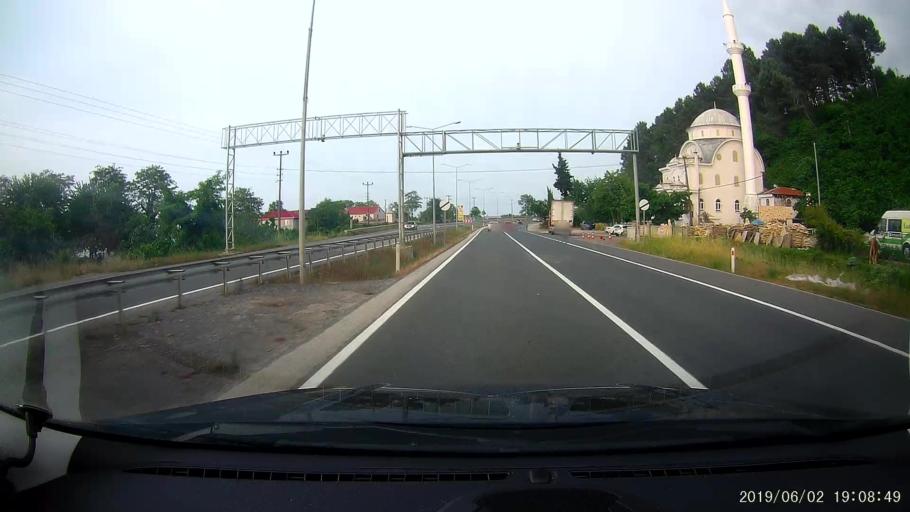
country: TR
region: Ordu
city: Gulyali
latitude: 40.9763
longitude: 38.0168
